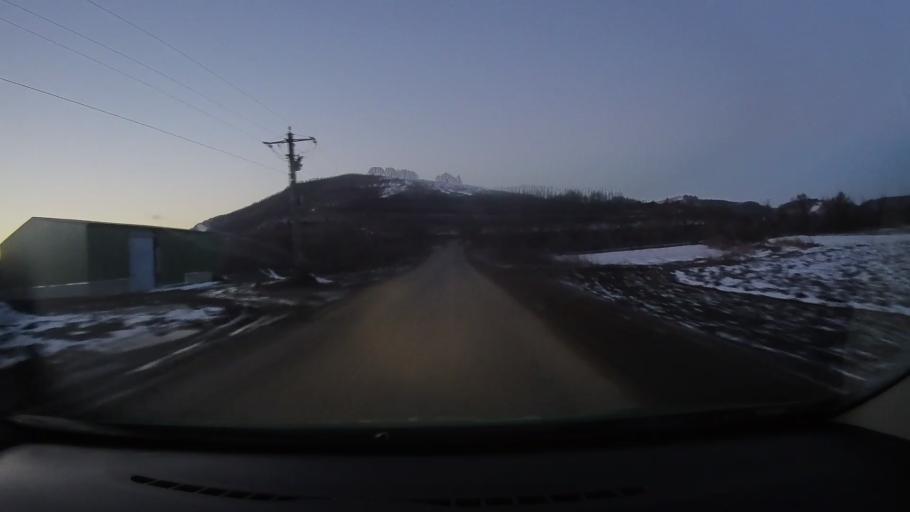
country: RO
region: Sibiu
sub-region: Comuna Alma
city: Alma
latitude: 46.2004
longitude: 24.4686
